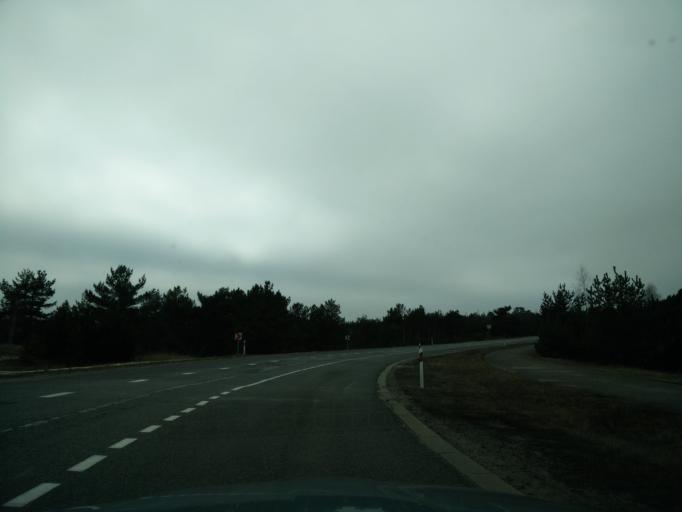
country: LT
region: Klaipedos apskritis
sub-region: Klaipeda
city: Klaipeda
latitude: 55.6825
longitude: 21.1293
